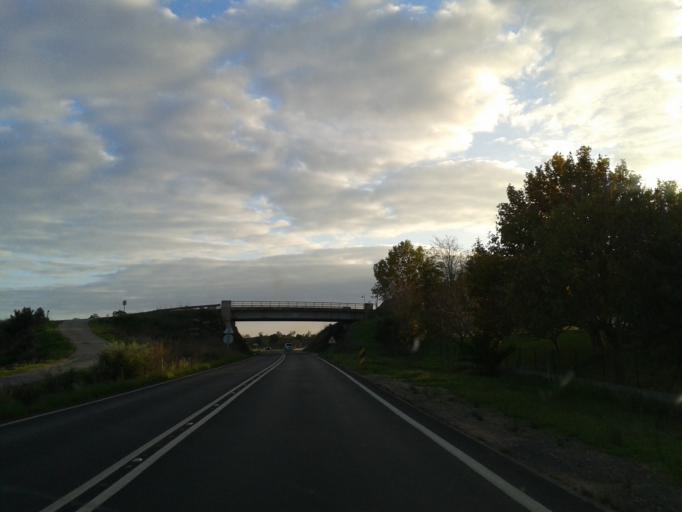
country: PT
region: Faro
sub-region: Castro Marim
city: Castro Marim
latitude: 37.2176
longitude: -7.4382
